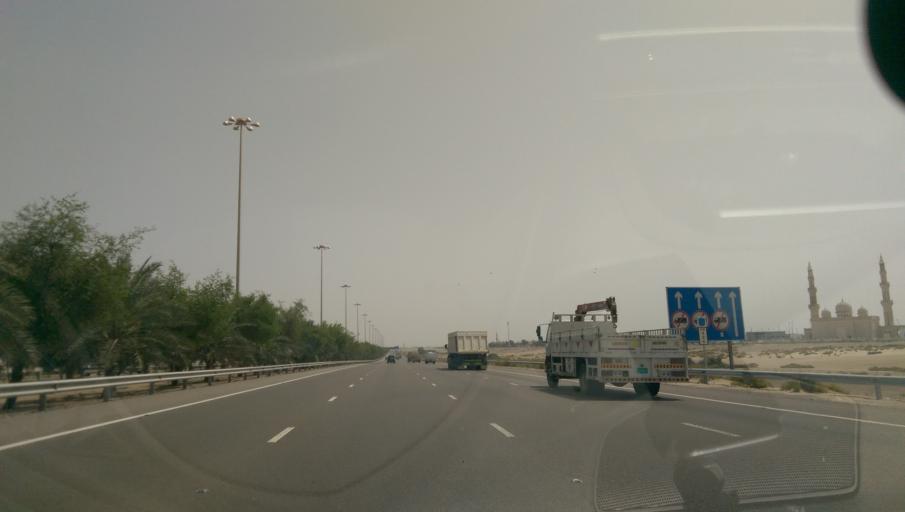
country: AE
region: Abu Dhabi
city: Abu Dhabi
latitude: 24.3489
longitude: 54.6428
